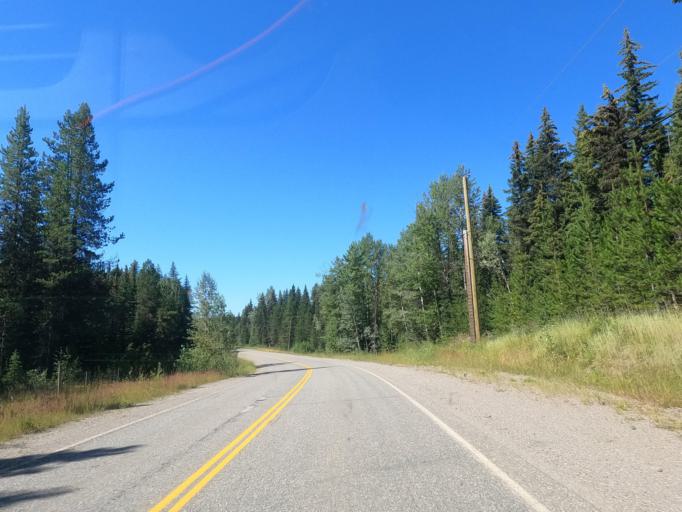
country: CA
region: British Columbia
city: Quesnel
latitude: 53.0427
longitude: -122.2553
